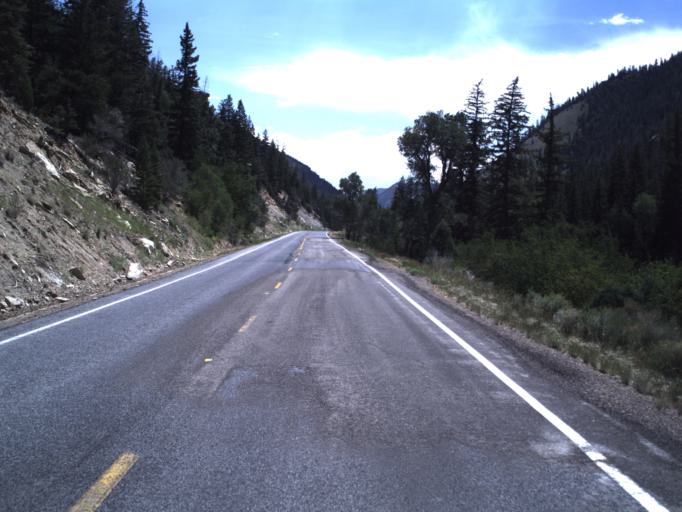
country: US
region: Utah
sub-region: Emery County
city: Huntington
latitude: 39.4533
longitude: -111.1416
